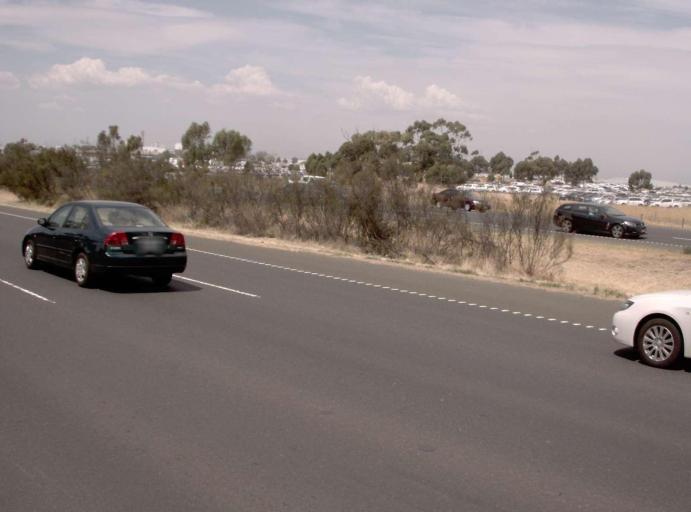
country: AU
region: Victoria
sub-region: Hobsons Bay
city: Laverton
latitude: -37.8374
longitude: 144.8000
